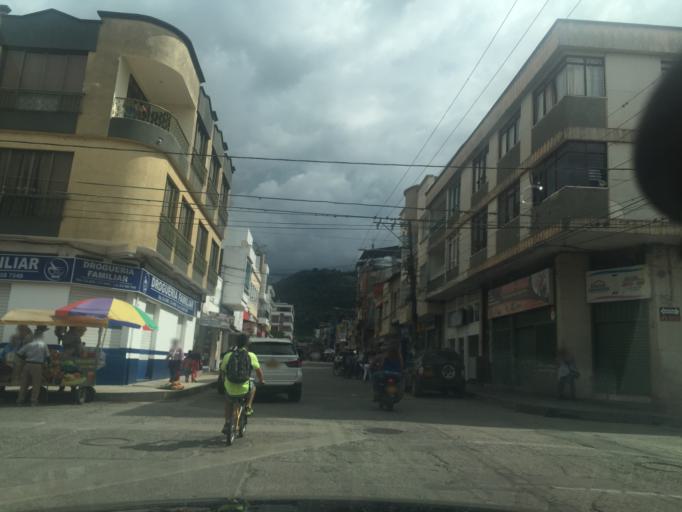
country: CO
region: Valle del Cauca
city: Caicedonia
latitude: 4.3330
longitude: -75.8297
